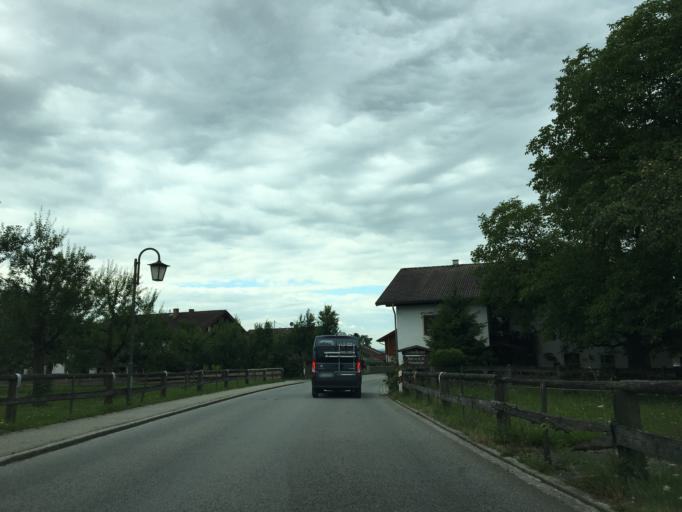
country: DE
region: Bavaria
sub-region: Upper Bavaria
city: Bad Feilnbach
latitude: 47.7743
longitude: 12.0127
